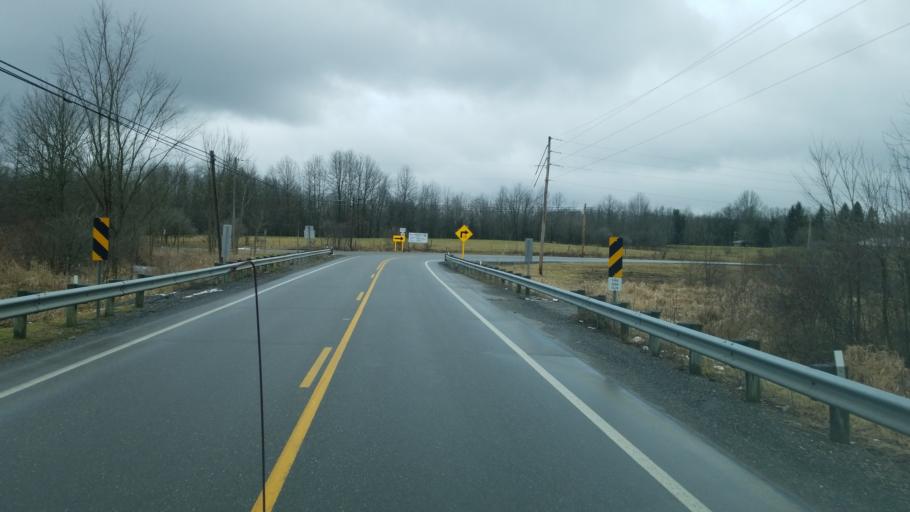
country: US
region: Ohio
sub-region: Trumbull County
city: Champion Heights
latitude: 41.3401
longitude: -80.9545
